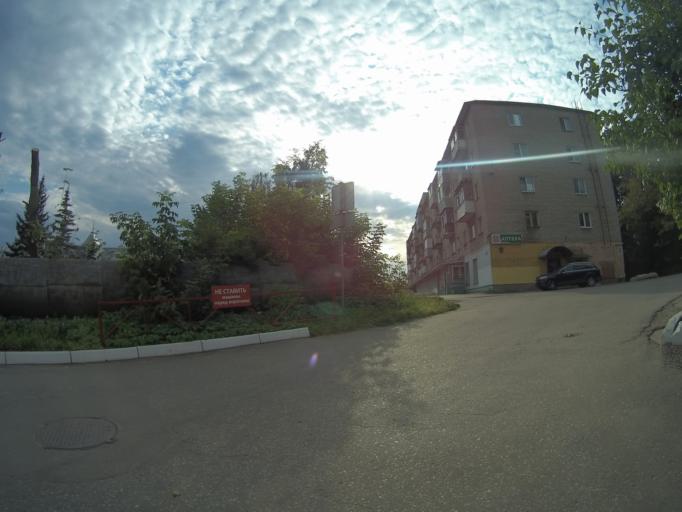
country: RU
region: Vladimir
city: Kommunar
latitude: 56.1384
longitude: 40.4315
